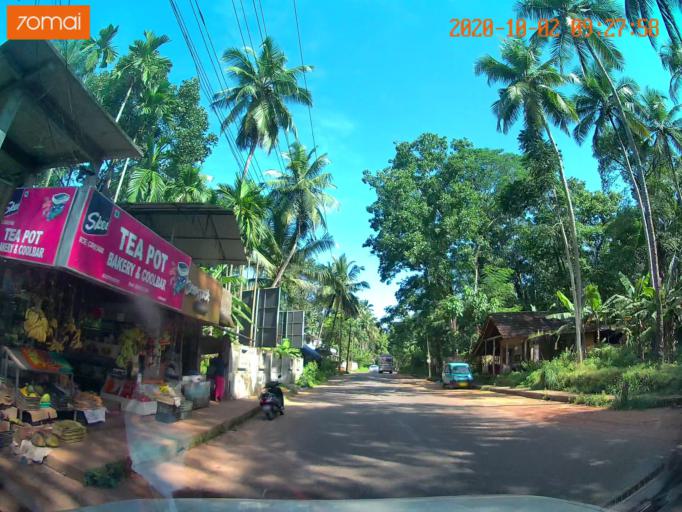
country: IN
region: Kerala
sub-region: Kozhikode
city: Naduvannur
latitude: 11.6028
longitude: 75.7641
